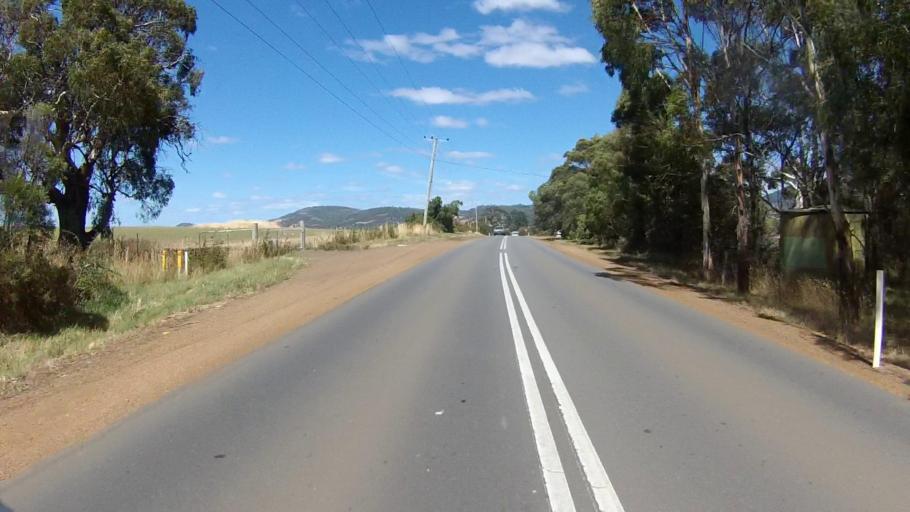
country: AU
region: Tasmania
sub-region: Clarence
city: Cambridge
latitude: -42.7469
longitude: 147.4184
